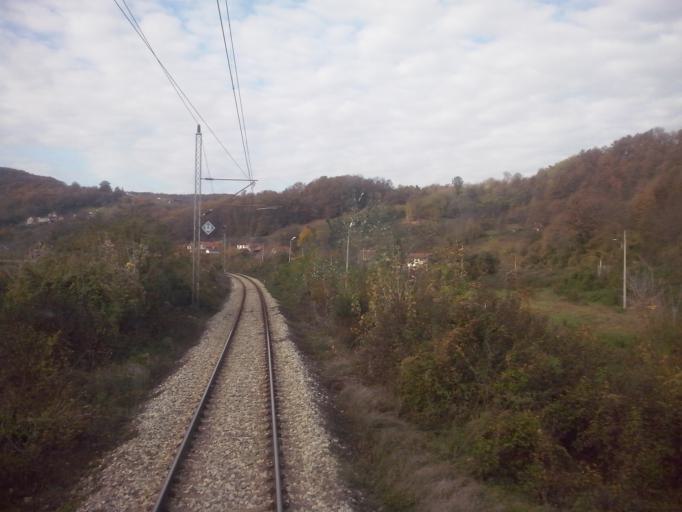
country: RS
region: Central Serbia
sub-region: Kolubarski Okrug
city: Lajkovac
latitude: 44.3410
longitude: 20.0835
